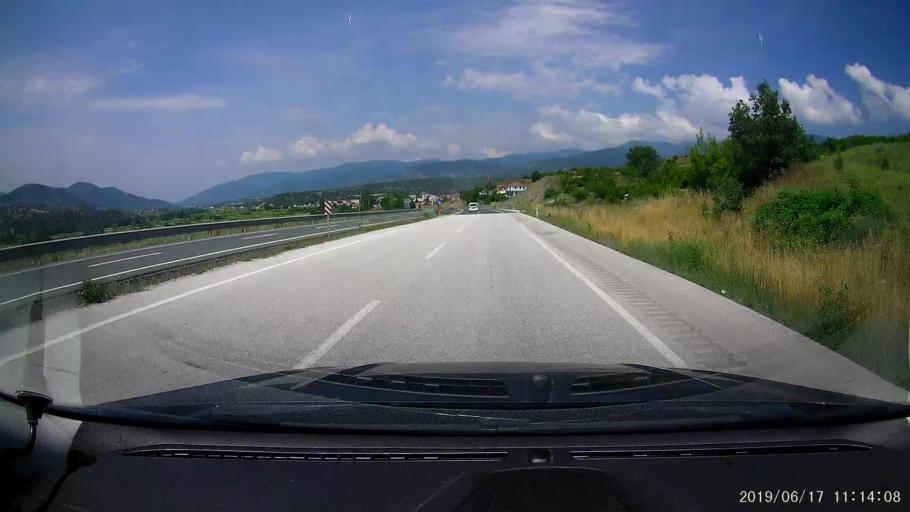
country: TR
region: Kastamonu
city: Tosya
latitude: 40.9570
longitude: 33.9558
